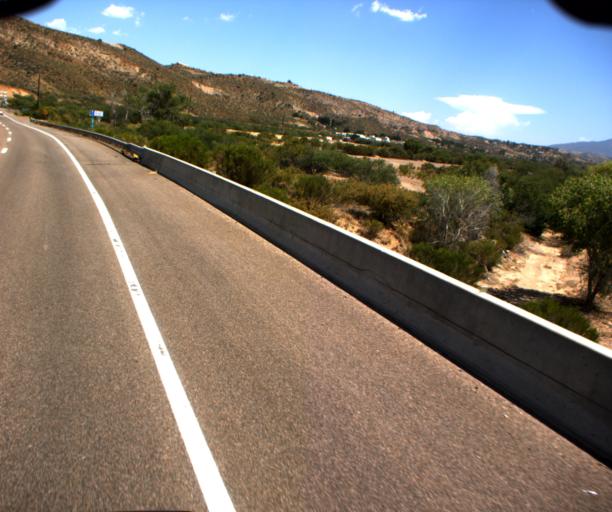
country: US
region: Arizona
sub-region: Gila County
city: Claypool
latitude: 33.4421
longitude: -110.8351
